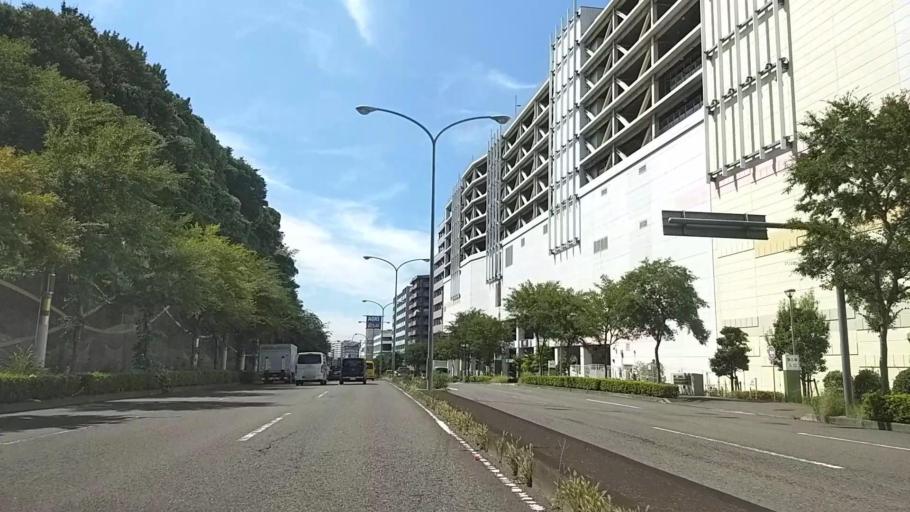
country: JP
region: Tokyo
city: Chofugaoka
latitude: 35.5525
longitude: 139.5803
